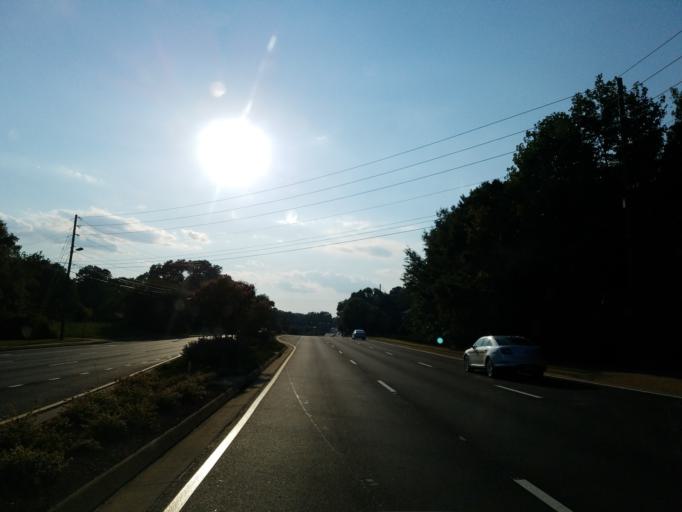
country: US
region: Georgia
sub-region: Fulton County
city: Alpharetta
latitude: 34.0705
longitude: -84.2879
